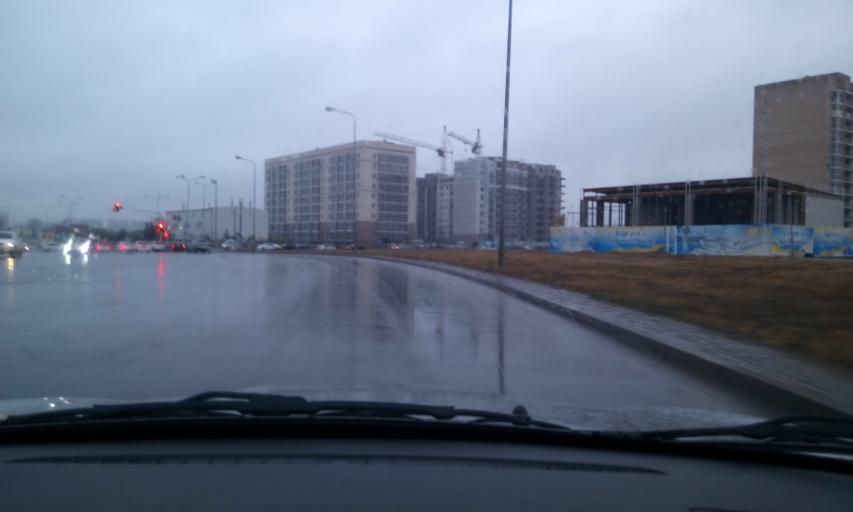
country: KZ
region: Astana Qalasy
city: Astana
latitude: 51.1248
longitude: 71.4872
